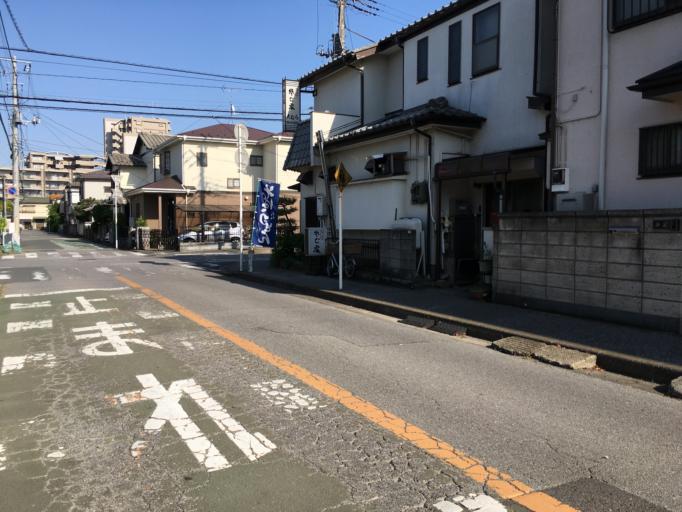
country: JP
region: Chiba
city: Nagareyama
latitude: 35.8197
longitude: 139.9152
